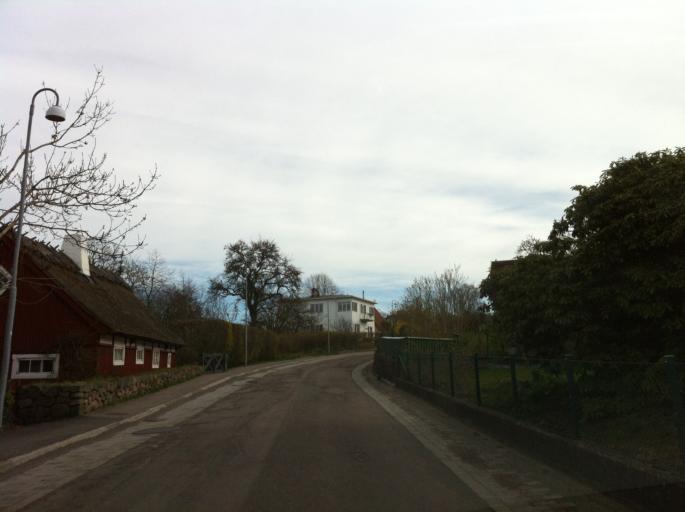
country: SE
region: Skane
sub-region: Hoganas Kommun
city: Hoganas
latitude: 56.2725
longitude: 12.5779
